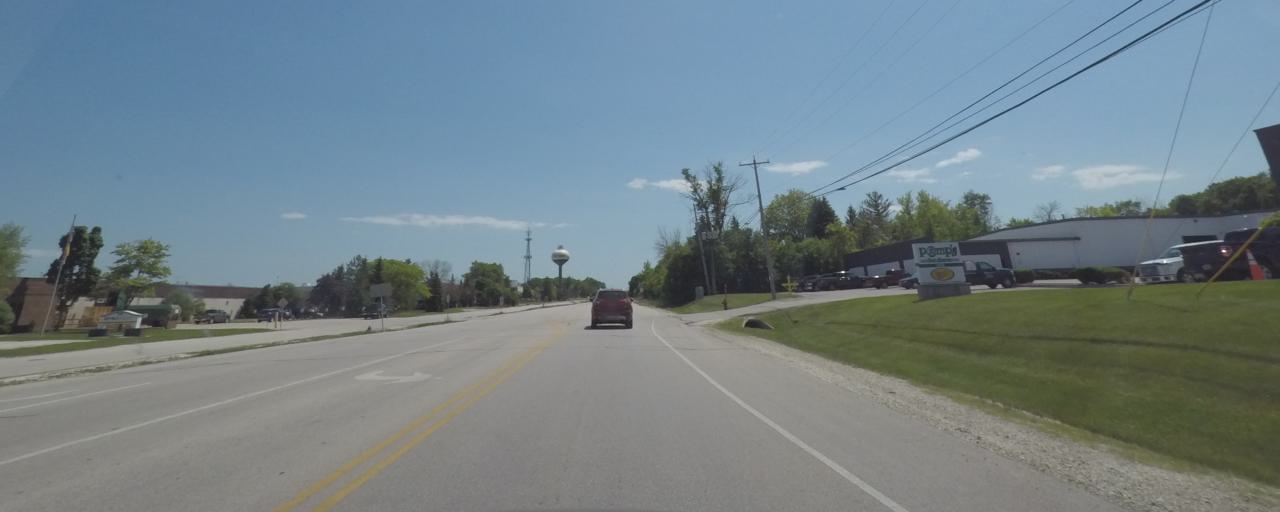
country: US
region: Wisconsin
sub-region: Waukesha County
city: New Berlin
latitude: 43.0021
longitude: -88.1276
